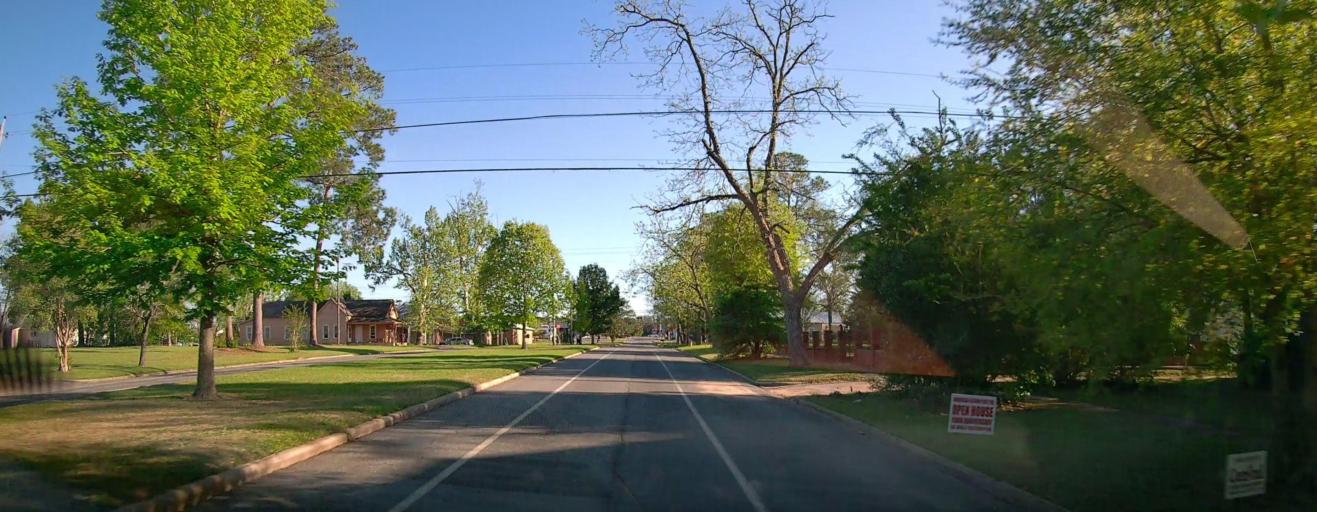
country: US
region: Georgia
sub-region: Ben Hill County
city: Fitzgerald
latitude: 31.7181
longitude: -83.2546
